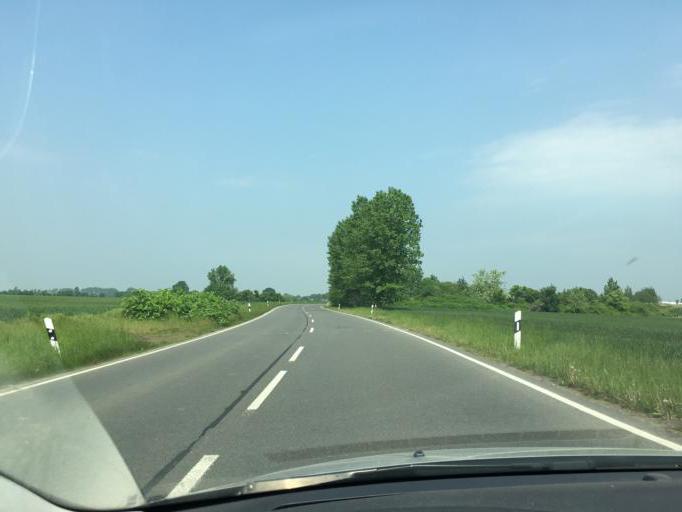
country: DE
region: Saxony
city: Naunhof
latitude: 51.2777
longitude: 12.5751
